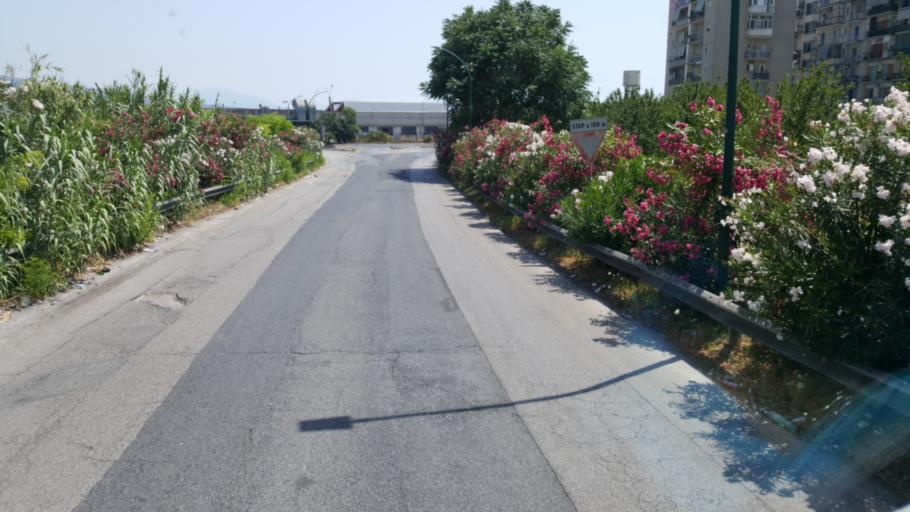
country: IT
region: Campania
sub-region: Provincia di Napoli
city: Arpino
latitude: 40.8828
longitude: 14.3169
